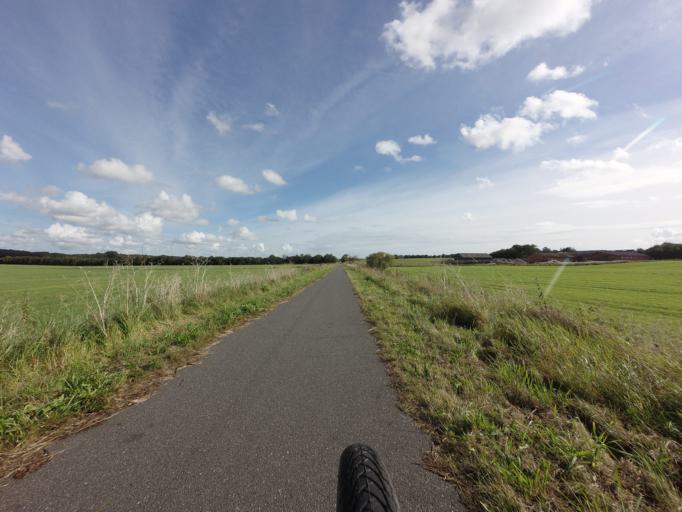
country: DK
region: Central Jutland
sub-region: Favrskov Kommune
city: Ulstrup
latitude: 56.5005
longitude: 9.7307
